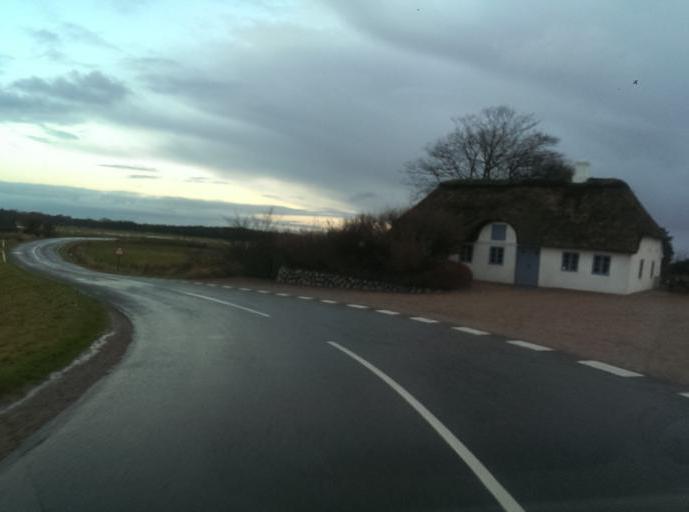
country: DK
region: South Denmark
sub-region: Esbjerg Kommune
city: Tjaereborg
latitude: 55.4587
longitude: 8.6389
